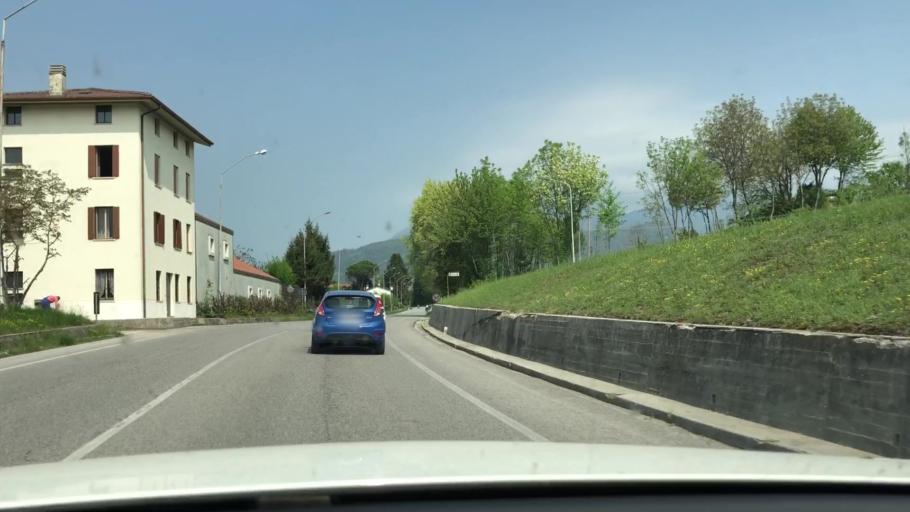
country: IT
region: Friuli Venezia Giulia
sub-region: Provincia di Udine
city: Cassacco
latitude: 46.1963
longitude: 13.1932
